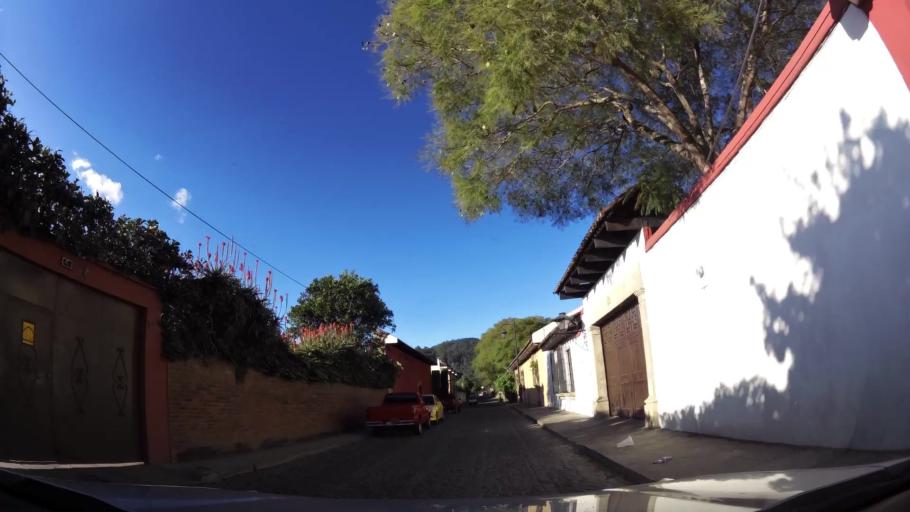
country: GT
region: Sacatepequez
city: Antigua Guatemala
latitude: 14.5556
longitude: -90.7286
